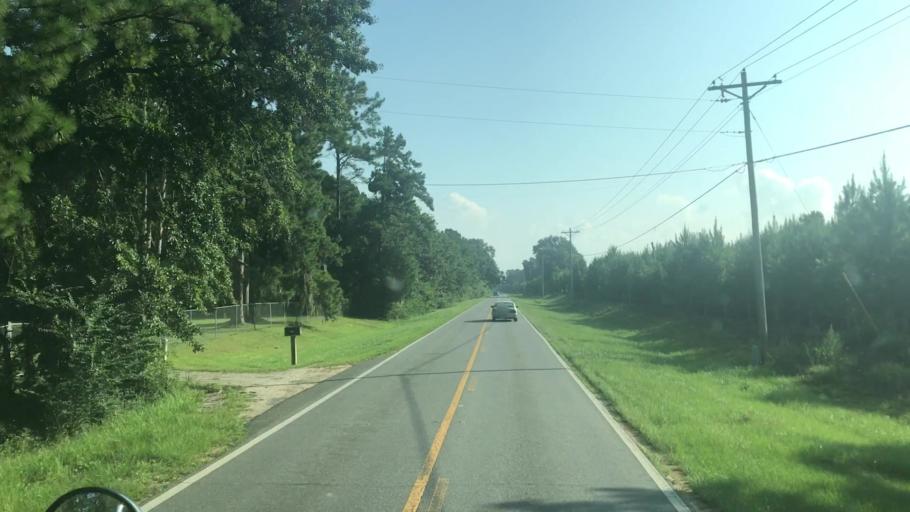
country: US
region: Florida
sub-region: Gadsden County
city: Quincy
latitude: 30.6375
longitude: -84.5763
